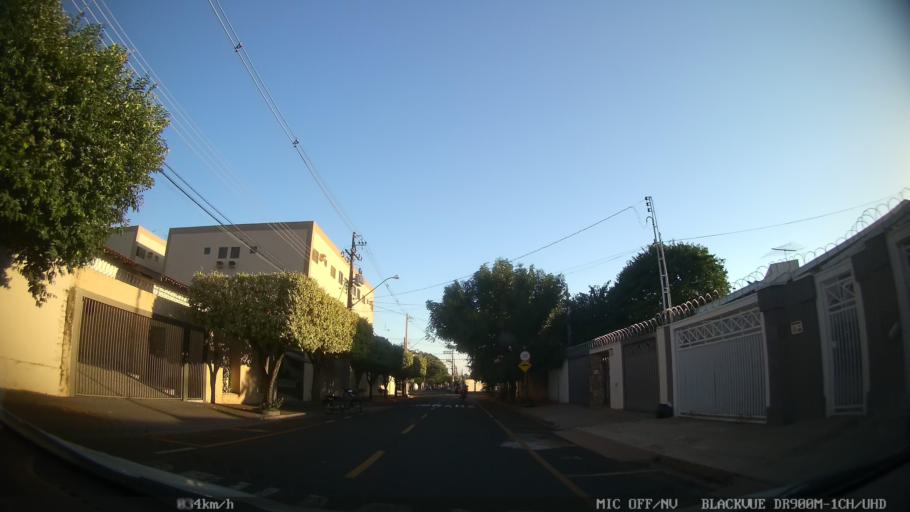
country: BR
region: Sao Paulo
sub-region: Sao Jose Do Rio Preto
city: Sao Jose do Rio Preto
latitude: -20.7913
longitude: -49.3635
